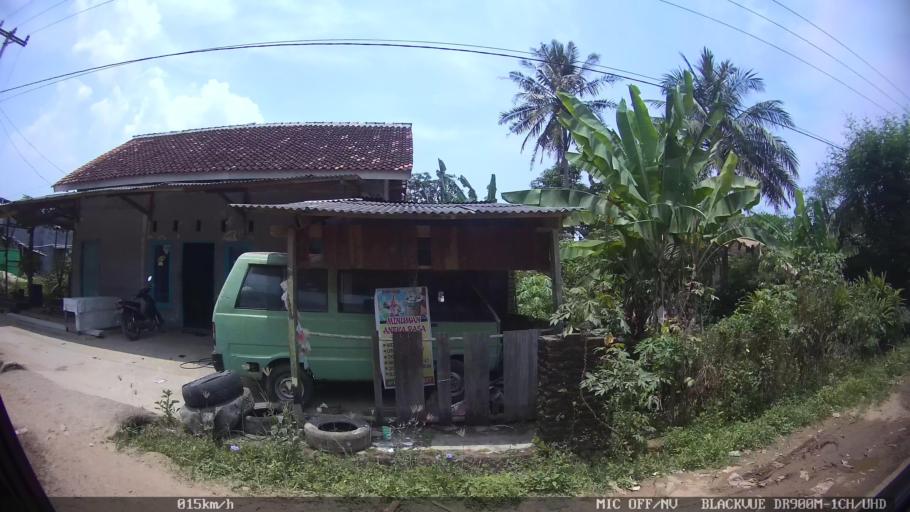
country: ID
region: Lampung
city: Kedaton
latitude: -5.3283
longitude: 105.2493
